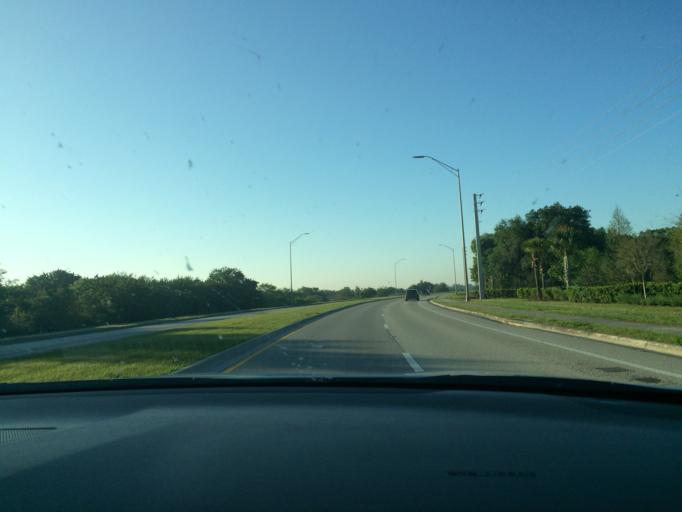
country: US
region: Florida
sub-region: Manatee County
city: Ellenton
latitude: 27.4699
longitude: -82.4320
